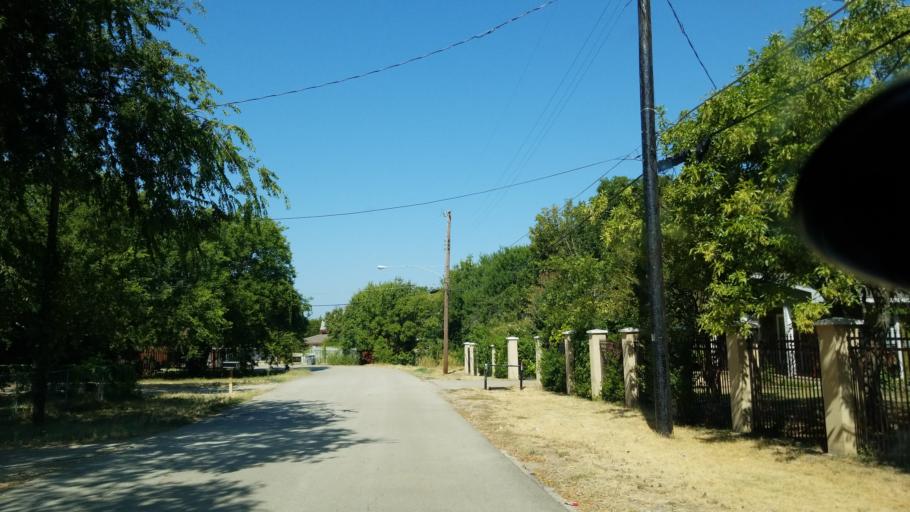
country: US
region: Texas
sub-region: Dallas County
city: Duncanville
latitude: 32.7000
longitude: -96.9222
